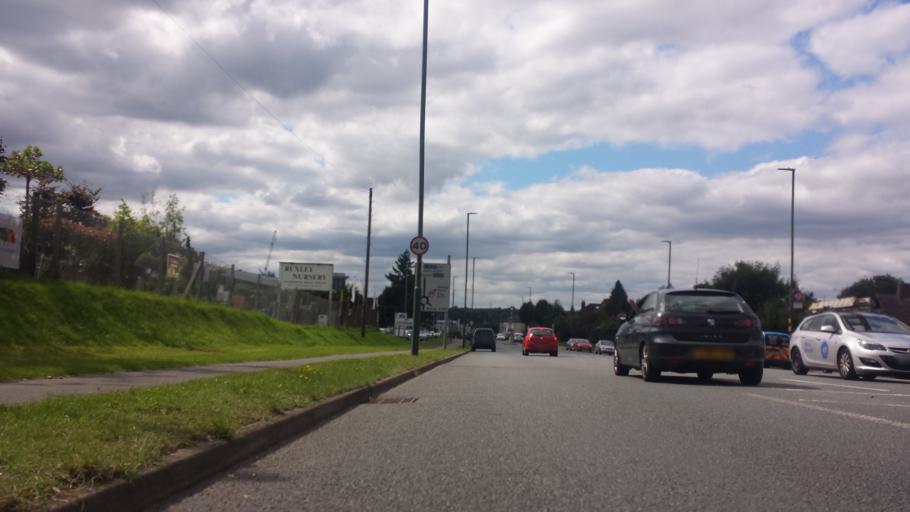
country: GB
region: England
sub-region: Greater London
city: Sidcup
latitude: 51.4146
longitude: 0.1314
